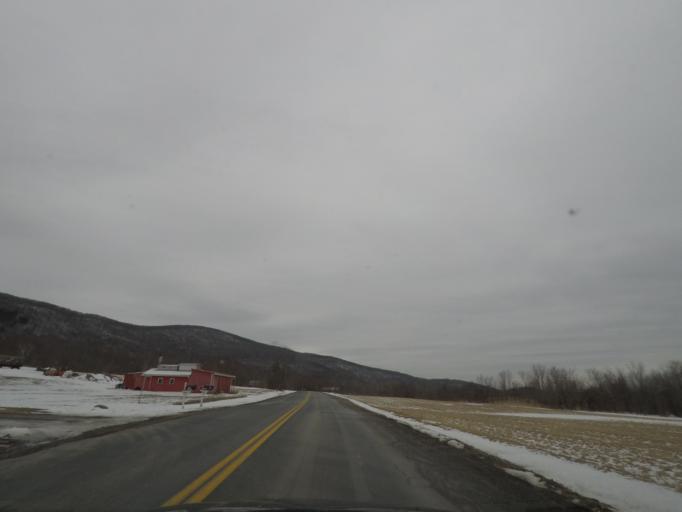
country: US
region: Massachusetts
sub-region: Berkshire County
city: Lanesborough
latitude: 42.5879
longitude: -73.3551
